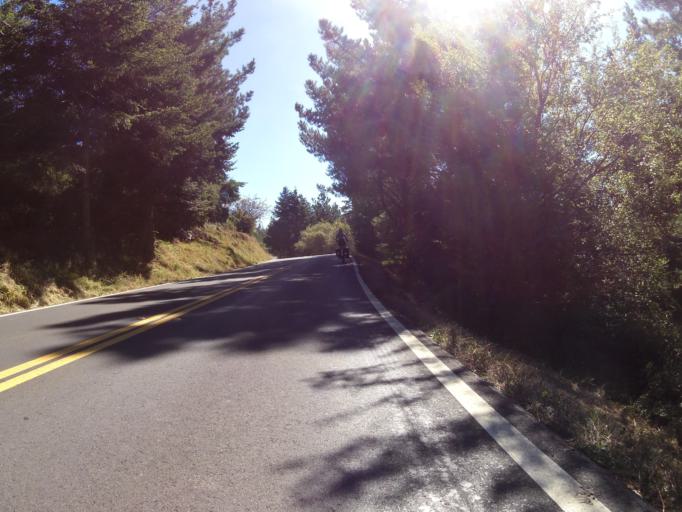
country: US
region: California
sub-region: Mendocino County
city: Fort Bragg
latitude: 39.6313
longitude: -123.7825
